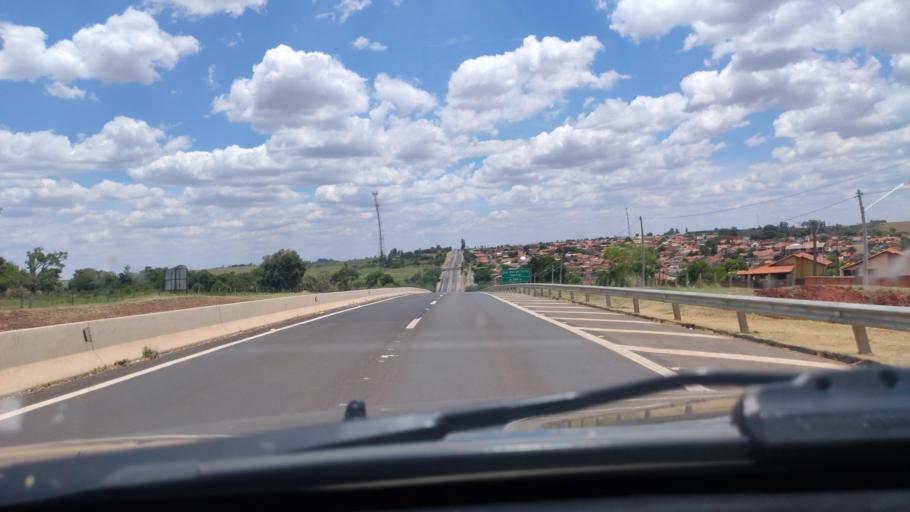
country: BR
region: Sao Paulo
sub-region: Duartina
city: Duartina
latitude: -22.6919
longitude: -49.4237
